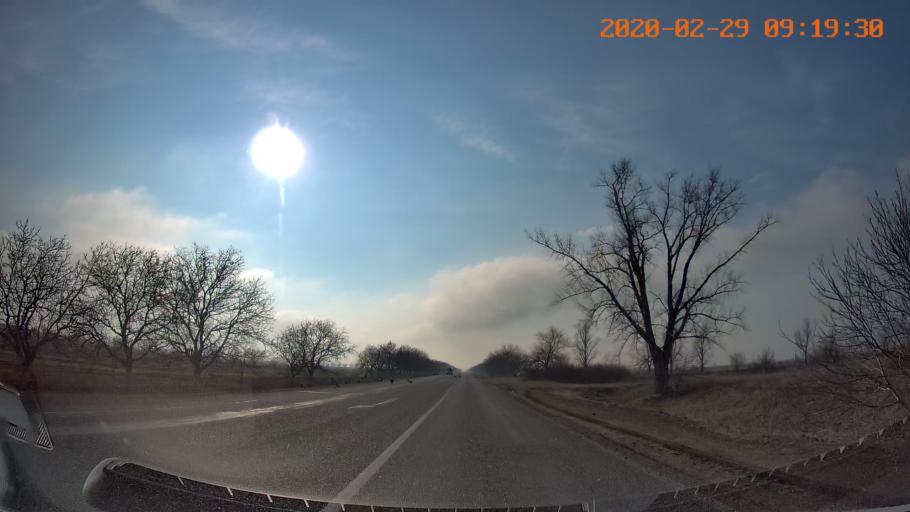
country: MD
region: Telenesti
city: Pervomaisc
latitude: 46.7618
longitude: 29.9397
